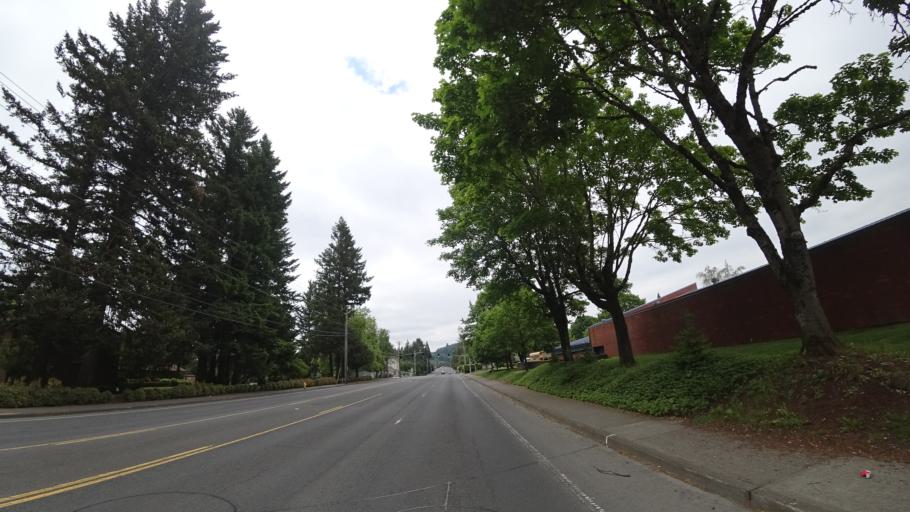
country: US
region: Oregon
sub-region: Multnomah County
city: Gresham
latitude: 45.4966
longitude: -122.4757
